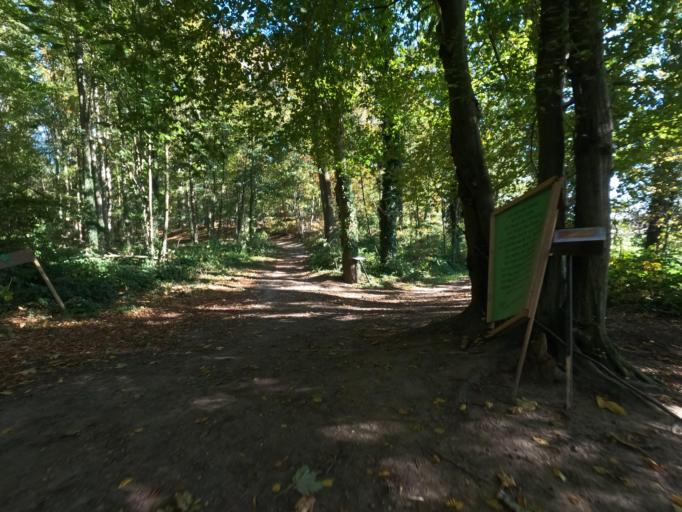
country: DE
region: North Rhine-Westphalia
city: Huckelhoven
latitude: 51.0539
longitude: 6.2409
